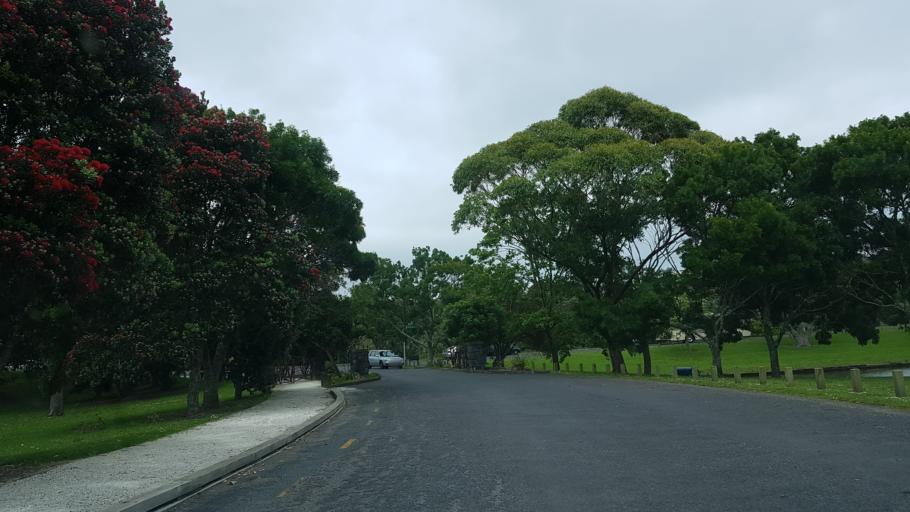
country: NZ
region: Auckland
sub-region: Auckland
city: North Shore
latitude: -36.8105
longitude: 174.7505
